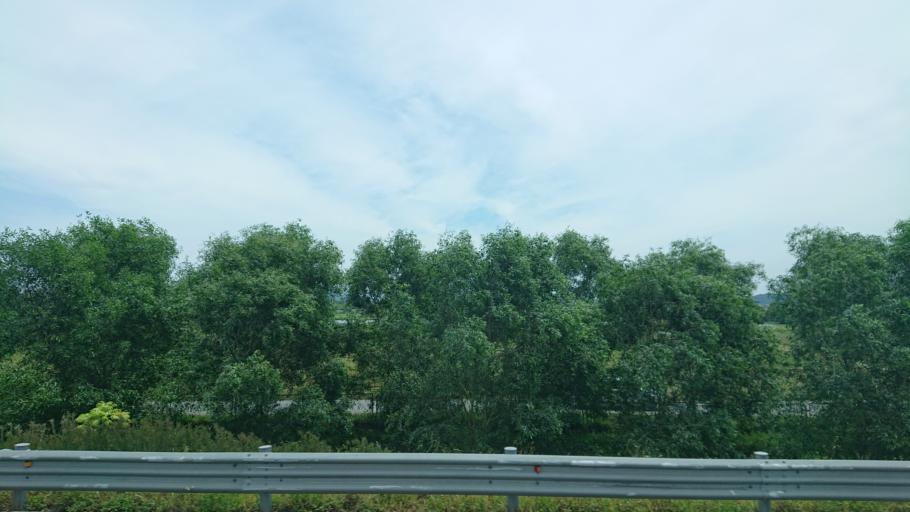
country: VN
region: Hai Phong
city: Tien Lang
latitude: 20.7710
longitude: 106.5892
